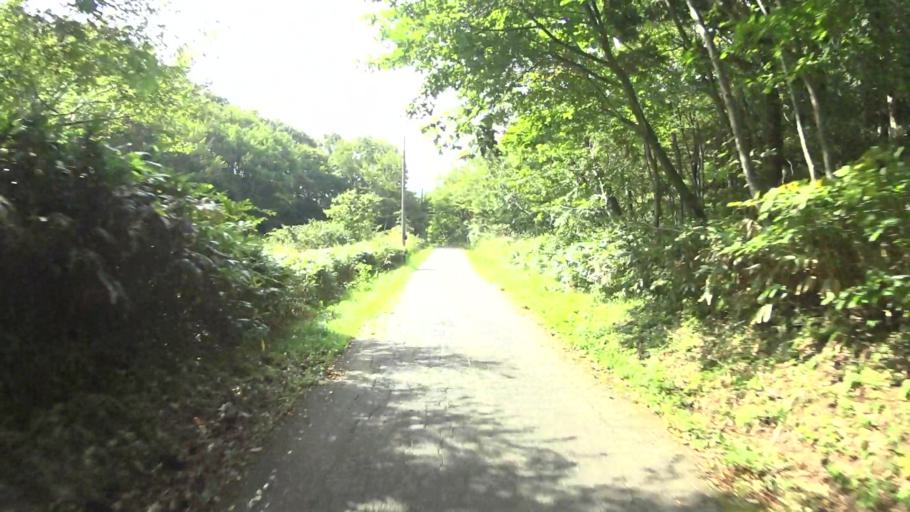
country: JP
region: Kyoto
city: Miyazu
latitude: 35.6505
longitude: 135.1804
